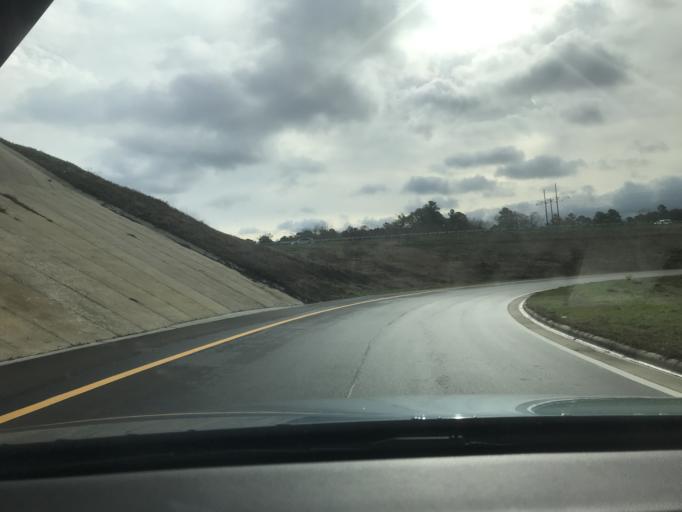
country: US
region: North Carolina
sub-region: Cumberland County
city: Fort Bragg
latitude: 35.1110
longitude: -78.9726
